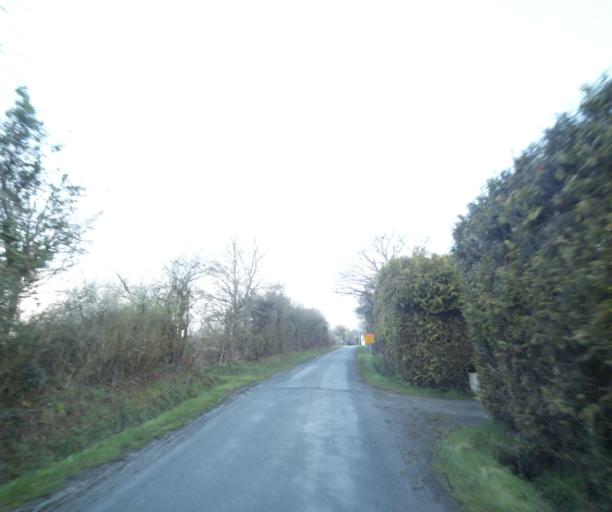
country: FR
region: Pays de la Loire
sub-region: Departement de la Loire-Atlantique
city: Savenay
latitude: 47.3880
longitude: -1.9057
